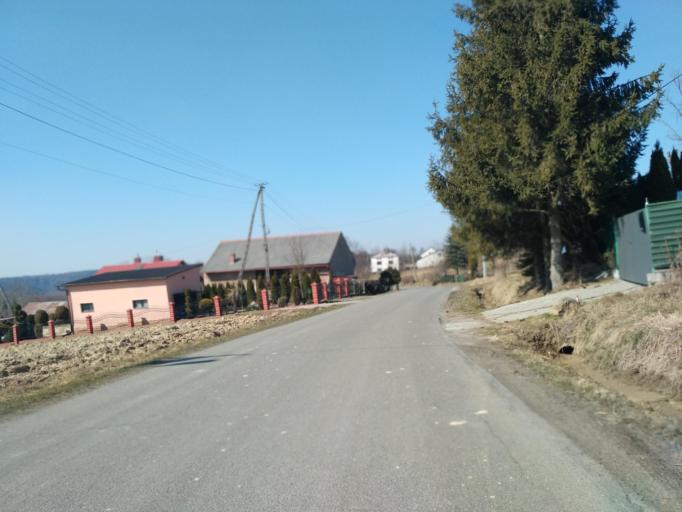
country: PL
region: Subcarpathian Voivodeship
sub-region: Powiat strzyzowski
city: Czudec
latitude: 49.9637
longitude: 21.8243
